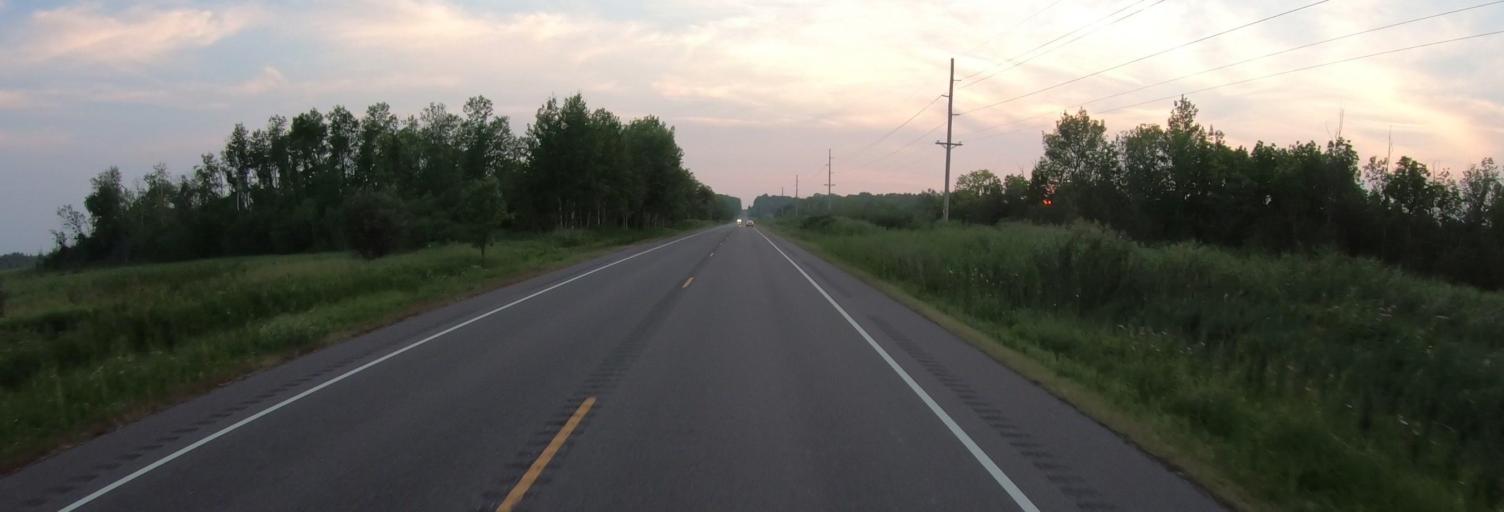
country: US
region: Minnesota
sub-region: Pine County
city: Rock Creek
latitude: 45.7735
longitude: -92.8336
